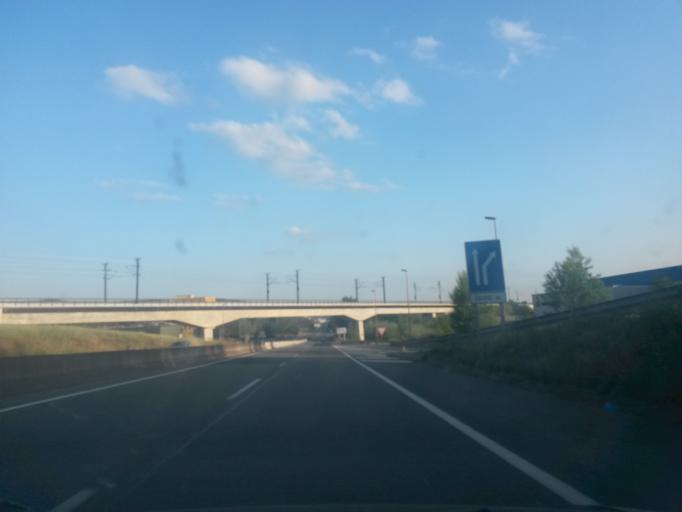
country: ES
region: Catalonia
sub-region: Provincia de Girona
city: Sarria de Ter
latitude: 42.0415
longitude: 2.8217
